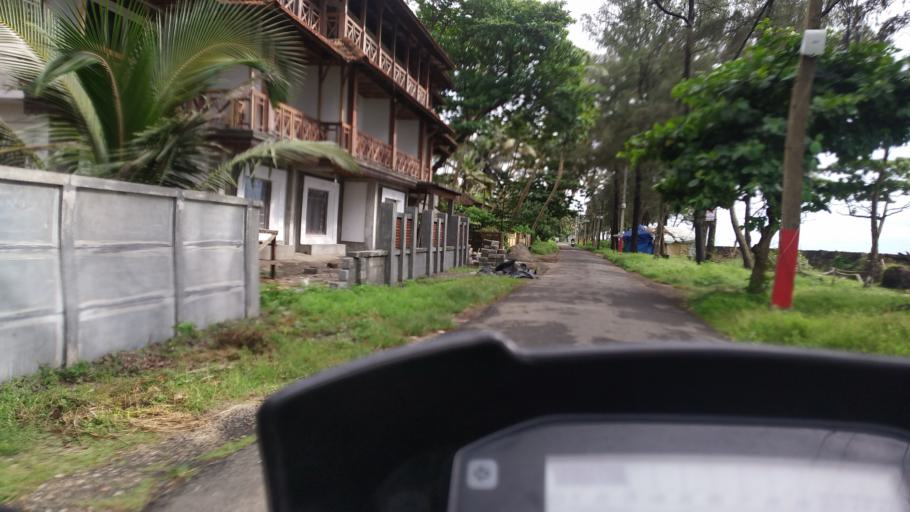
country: IN
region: Kerala
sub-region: Thrissur District
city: Kodungallur
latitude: 10.1594
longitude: 76.1723
